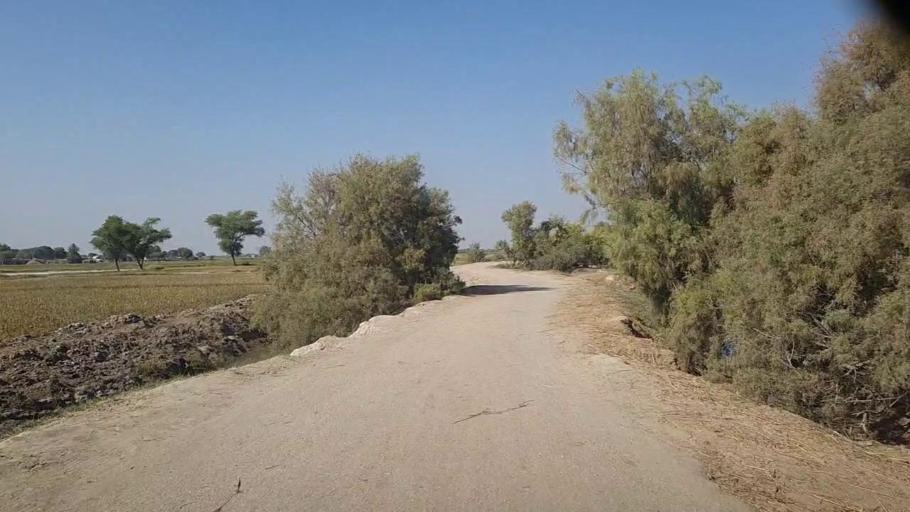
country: PK
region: Sindh
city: Tangwani
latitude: 28.2605
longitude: 68.9344
